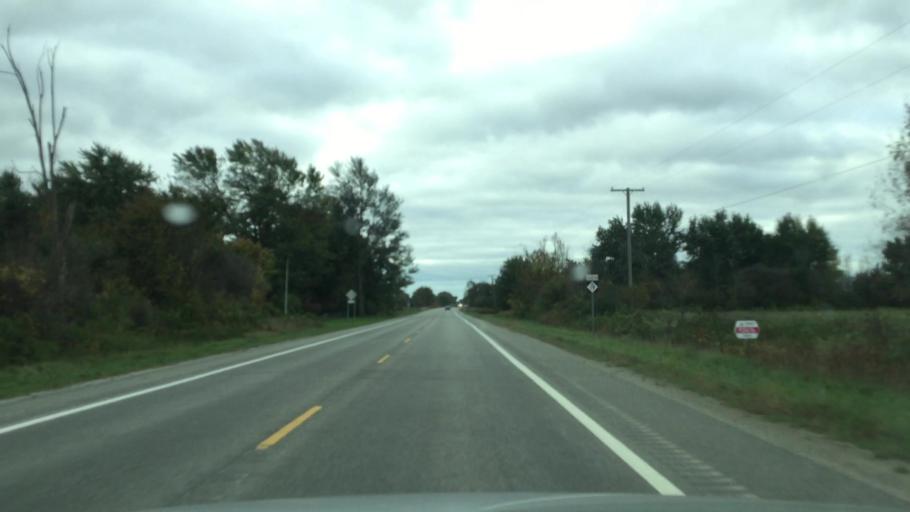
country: US
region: Michigan
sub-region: Macomb County
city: Memphis
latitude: 42.9696
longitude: -82.7640
